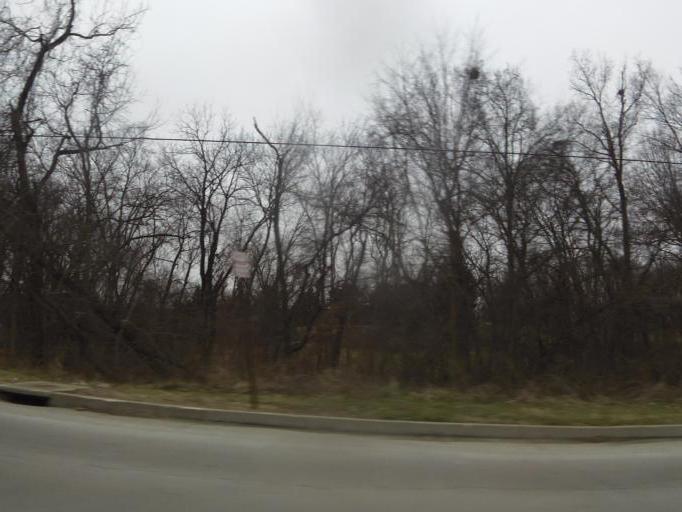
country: US
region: Missouri
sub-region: Marion County
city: Hannibal
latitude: 39.7192
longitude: -91.4006
